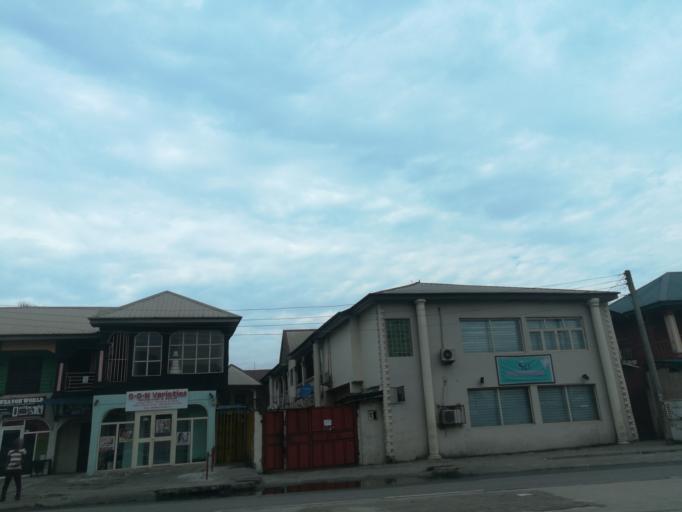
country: NG
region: Rivers
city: Port Harcourt
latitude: 4.8420
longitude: 6.9755
